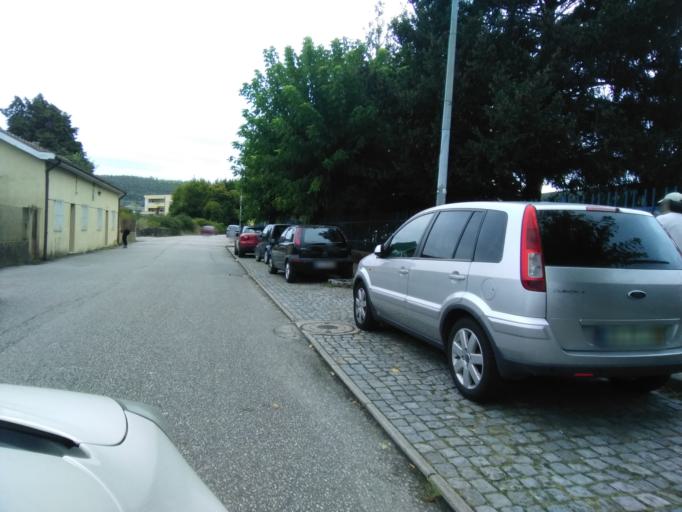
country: PT
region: Porto
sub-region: Valongo
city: Valongo
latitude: 41.1903
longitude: -8.4959
